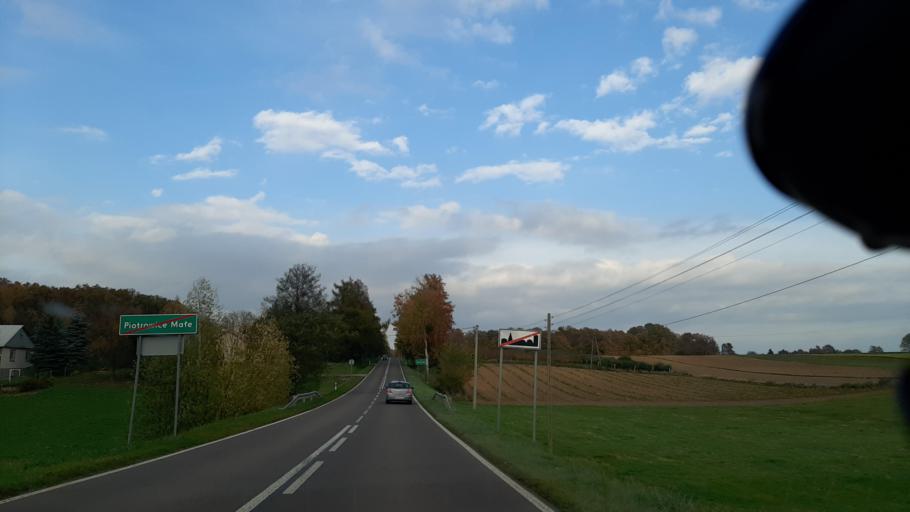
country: PL
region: Lublin Voivodeship
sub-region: Powiat pulawski
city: Naleczow
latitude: 51.3263
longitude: 22.2410
